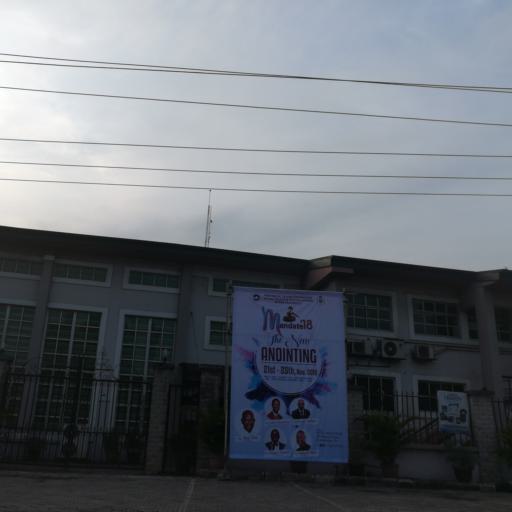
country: NG
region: Rivers
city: Port Harcourt
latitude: 4.8465
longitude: 7.0451
